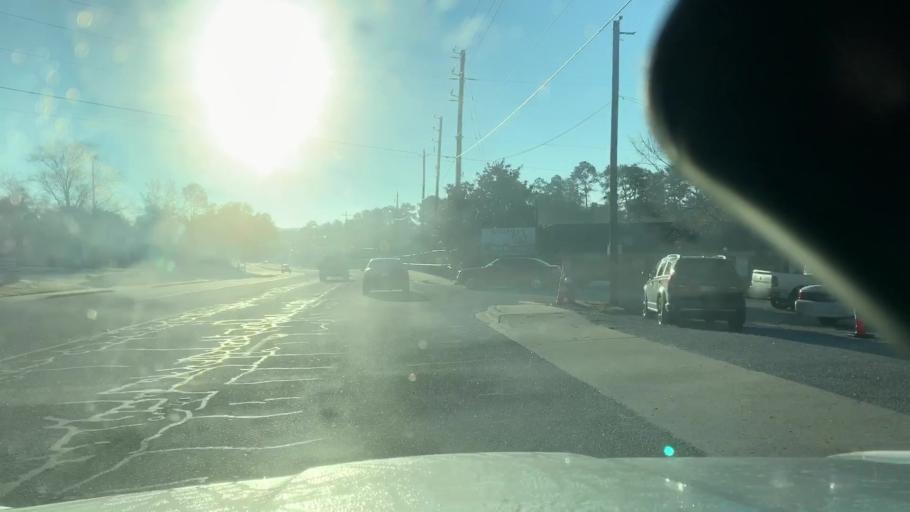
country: US
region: South Carolina
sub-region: Richland County
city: Woodfield
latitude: 34.0439
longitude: -80.9413
